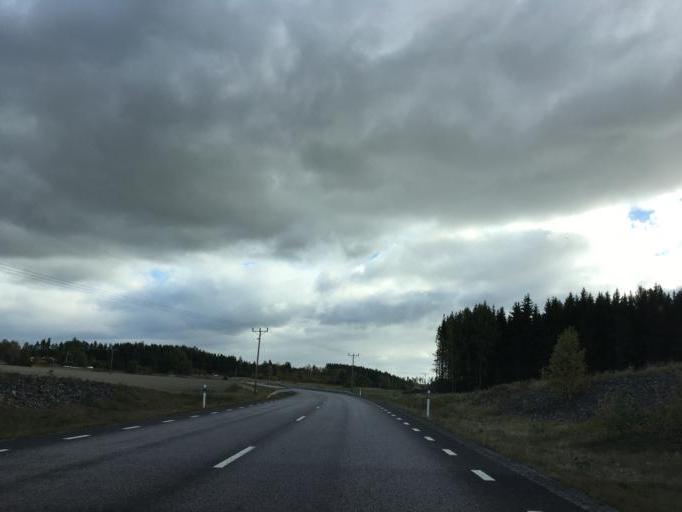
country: SE
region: Soedermanland
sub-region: Nykopings Kommun
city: Olstorp
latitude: 58.8969
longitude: 16.6427
